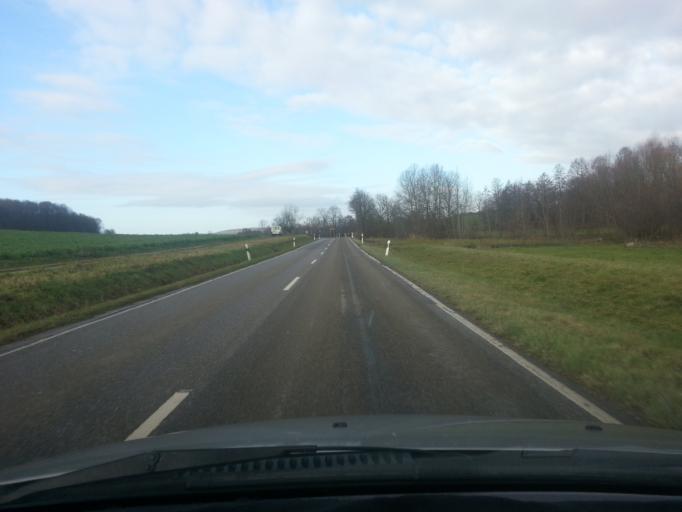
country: DE
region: Baden-Wuerttemberg
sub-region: Regierungsbezirk Stuttgart
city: Eppingen
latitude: 49.1560
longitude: 8.8866
